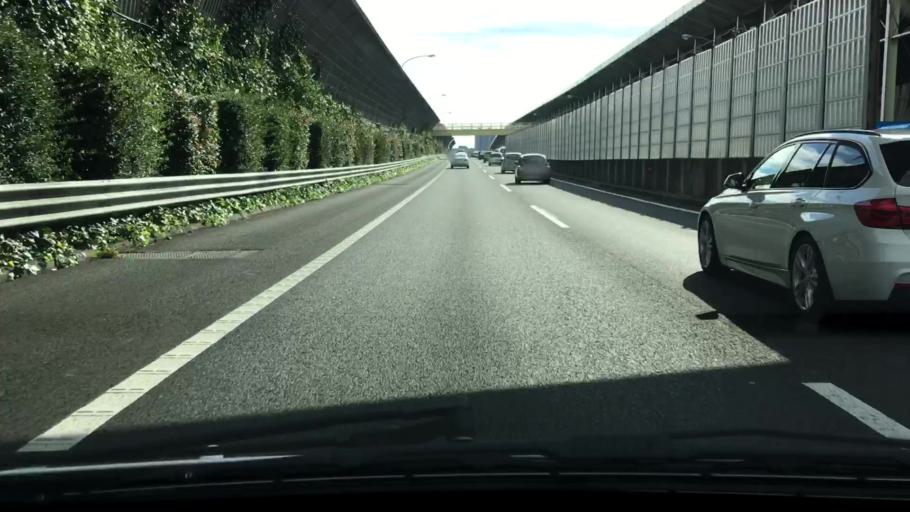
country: JP
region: Chiba
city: Chiba
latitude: 35.6388
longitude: 140.1177
